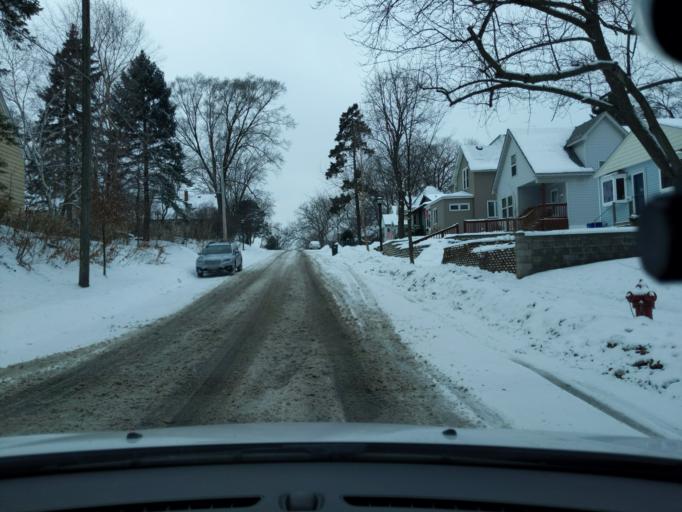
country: US
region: Minnesota
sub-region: Ramsey County
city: Falcon Heights
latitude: 44.9682
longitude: -93.1785
